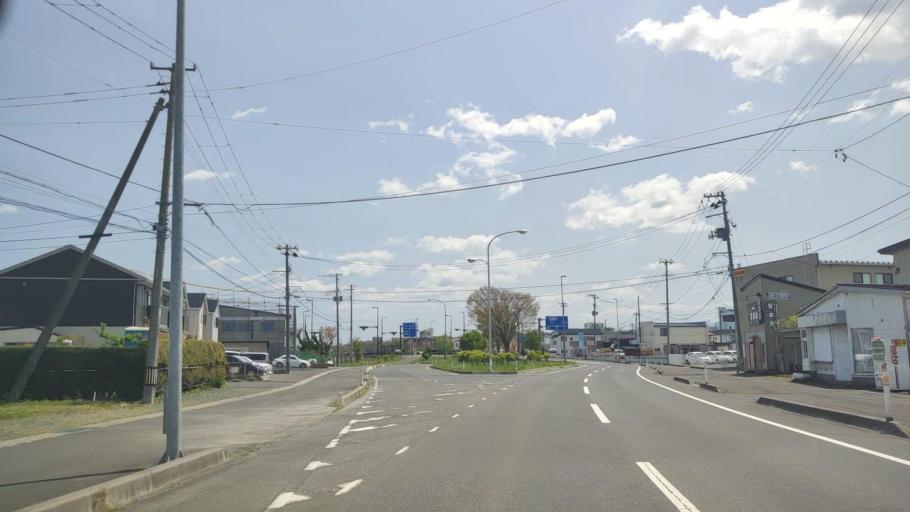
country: JP
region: Aomori
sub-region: Hachinohe Shi
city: Uchimaru
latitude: 40.5117
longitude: 141.4380
